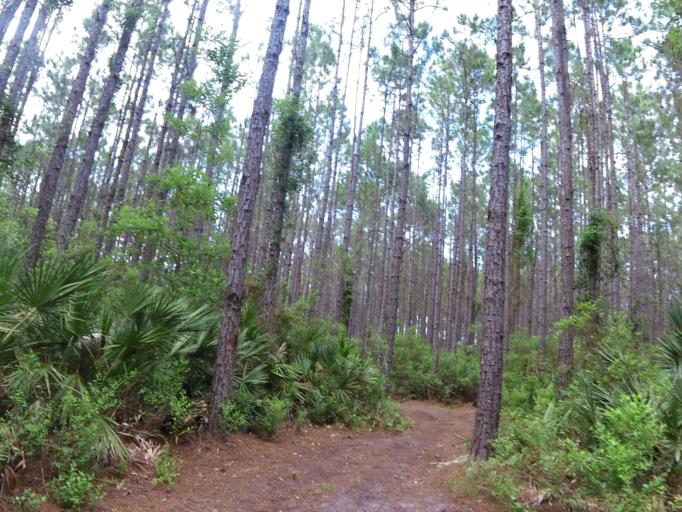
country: US
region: Florida
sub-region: Duval County
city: Atlantic Beach
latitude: 30.4560
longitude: -81.4700
